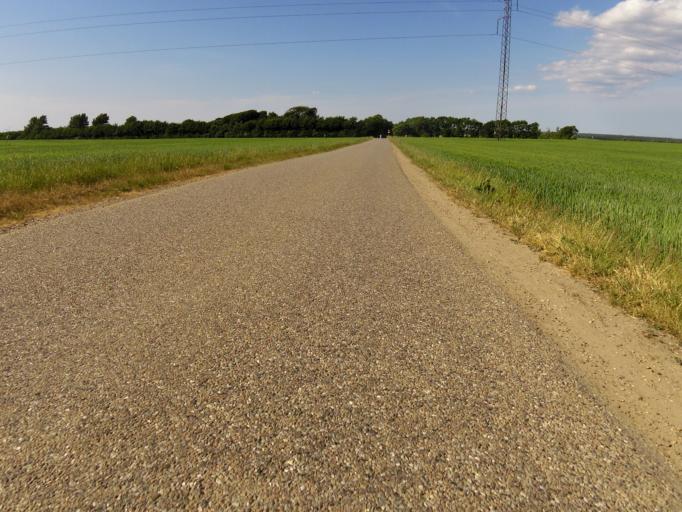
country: DK
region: Central Jutland
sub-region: Holstebro Kommune
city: Vinderup
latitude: 56.4597
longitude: 8.8484
